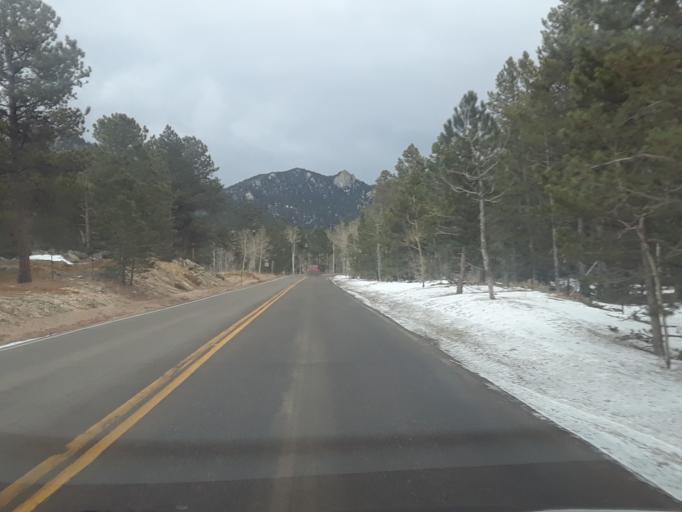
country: US
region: Colorado
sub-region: Gilpin County
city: Central City
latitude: 39.8416
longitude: -105.4562
